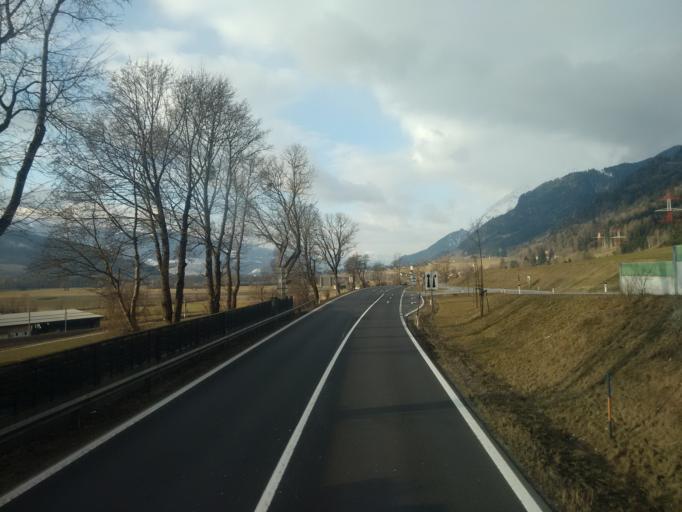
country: AT
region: Styria
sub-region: Politischer Bezirk Liezen
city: Worschach
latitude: 47.5465
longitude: 14.1346
